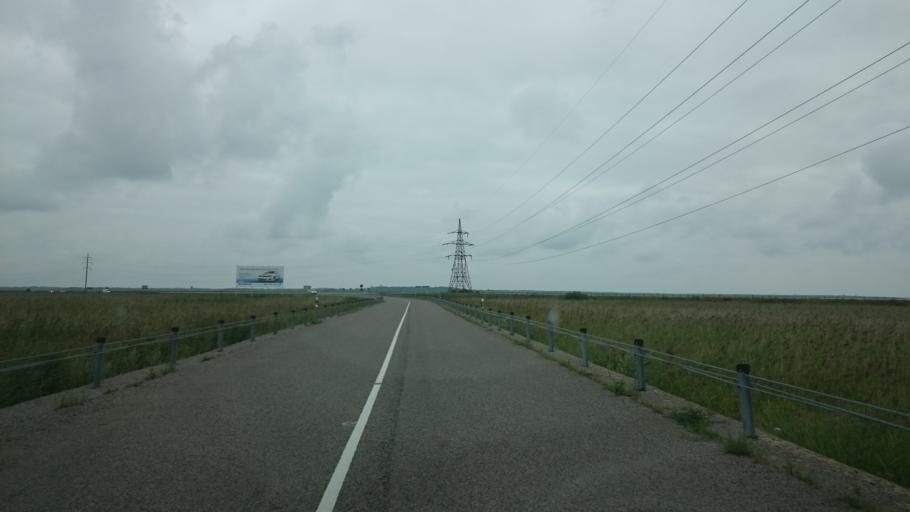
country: EE
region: Saare
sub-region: Orissaare vald
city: Orissaare
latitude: 58.5486
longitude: 23.1330
